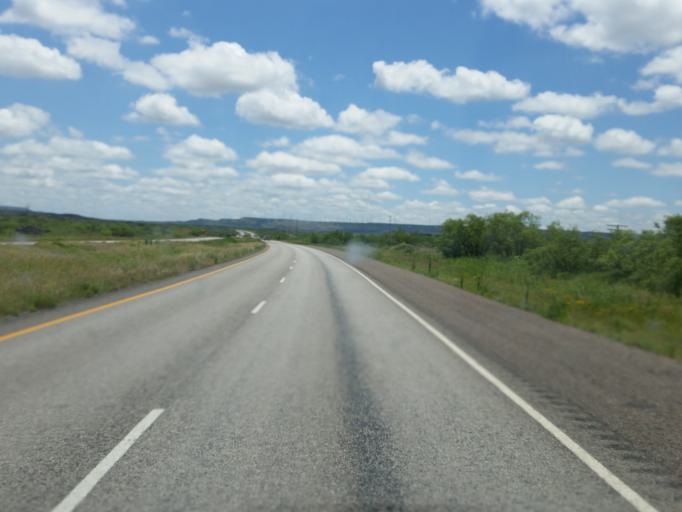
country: US
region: Texas
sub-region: Garza County
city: Post
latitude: 33.0141
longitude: -101.1763
